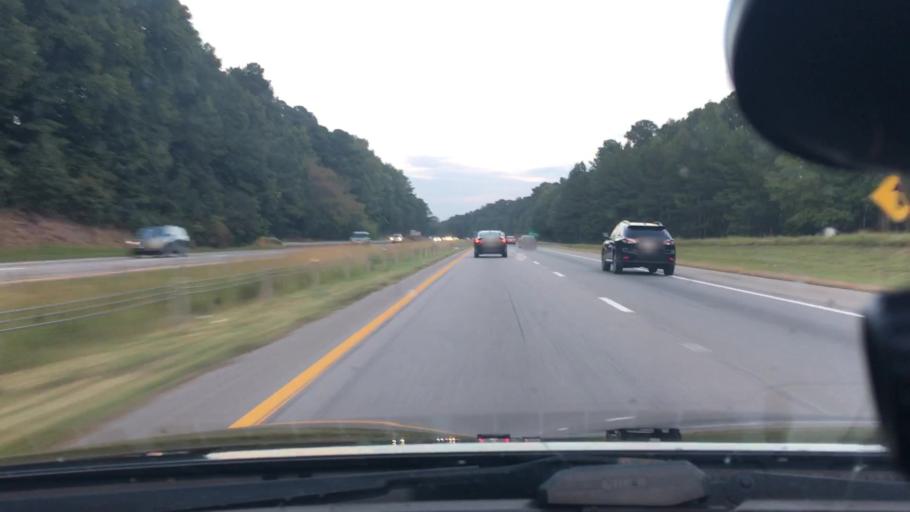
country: US
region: North Carolina
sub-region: Wake County
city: Apex
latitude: 35.7243
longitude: -78.8204
